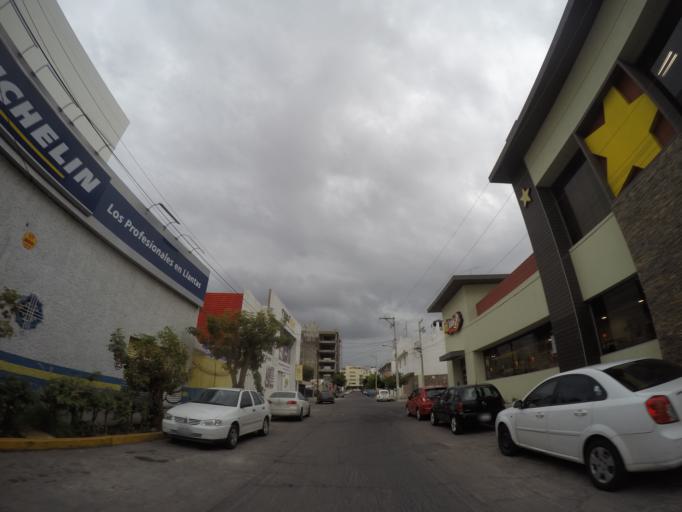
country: MX
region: San Luis Potosi
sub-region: San Luis Potosi
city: San Luis Potosi
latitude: 22.1481
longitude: -101.0172
